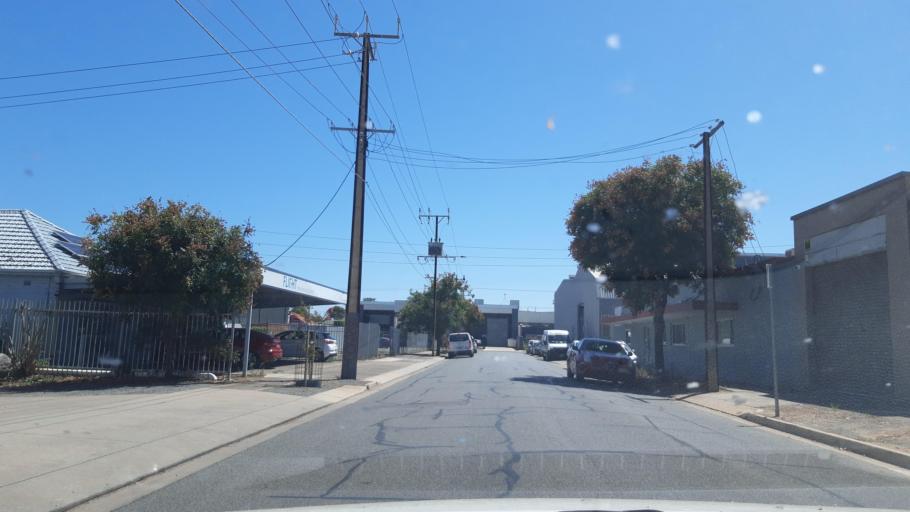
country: AU
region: South Australia
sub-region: Mitcham
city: Clarence Gardens
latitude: -34.9852
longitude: 138.5705
